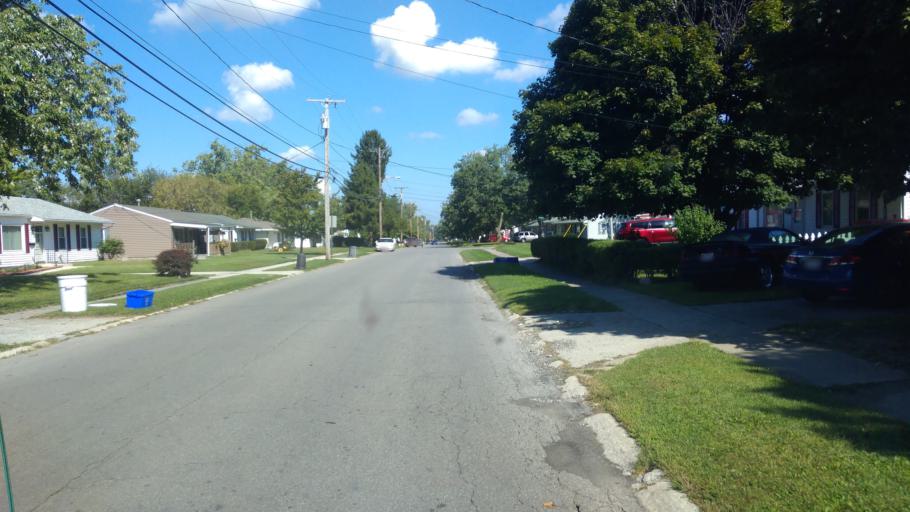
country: US
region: Ohio
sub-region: Marion County
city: Marion
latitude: 40.6016
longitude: -83.1201
